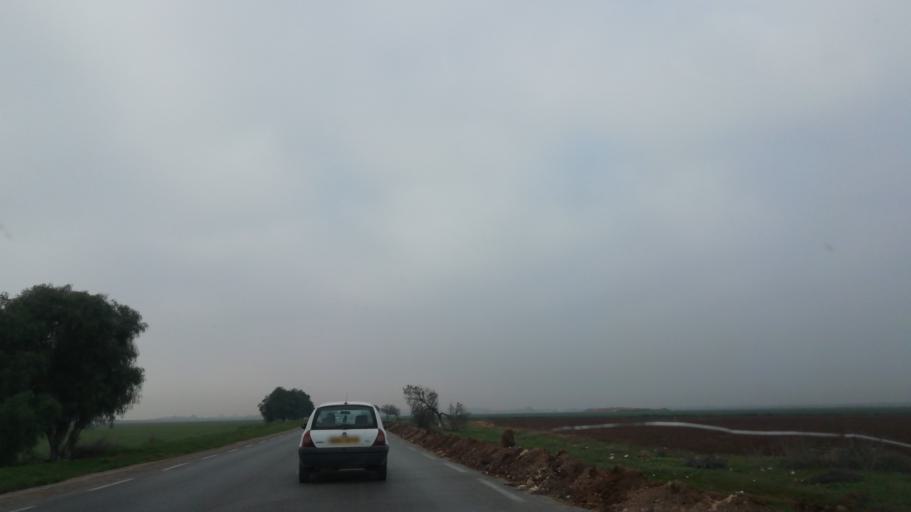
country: DZ
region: Relizane
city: Djidiouia
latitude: 35.9000
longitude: 0.7622
